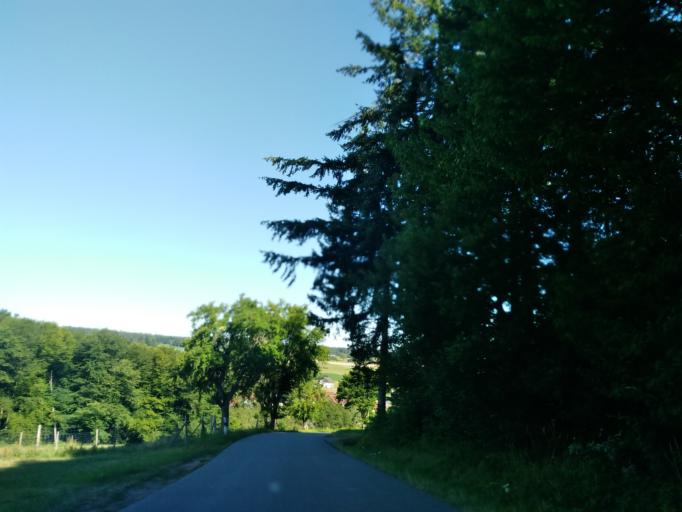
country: DE
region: Baden-Wuerttemberg
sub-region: Karlsruhe Region
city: Mudau
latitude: 49.5409
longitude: 9.2457
